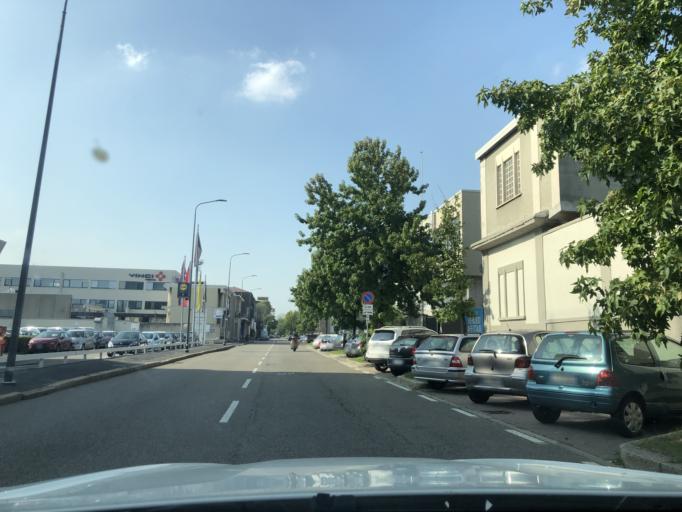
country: IT
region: Lombardy
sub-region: Citta metropolitana di Milano
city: Baranzate
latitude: 45.4989
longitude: 9.1270
